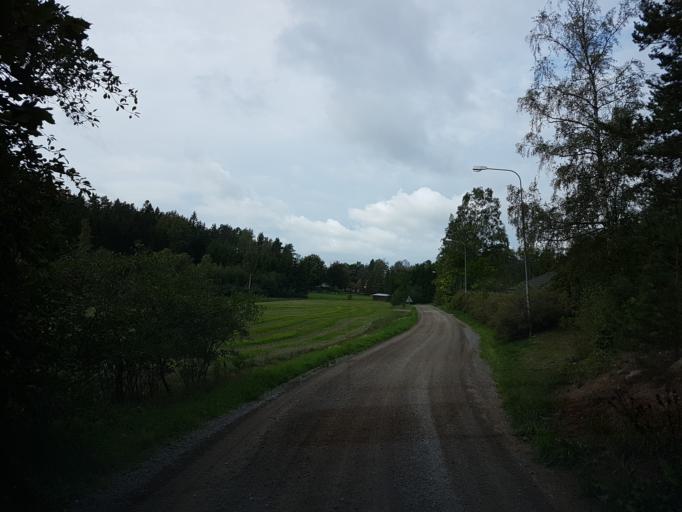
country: SE
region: OEstergoetland
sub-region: Atvidabergs Kommun
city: Atvidaberg
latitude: 58.2157
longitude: 16.0301
